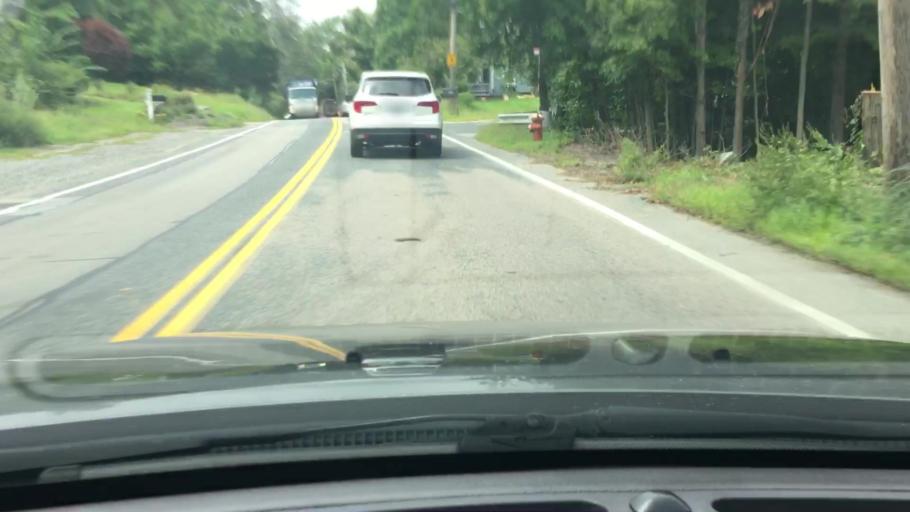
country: US
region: Massachusetts
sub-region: Middlesex County
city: Hopkinton
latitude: 42.2355
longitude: -71.5575
